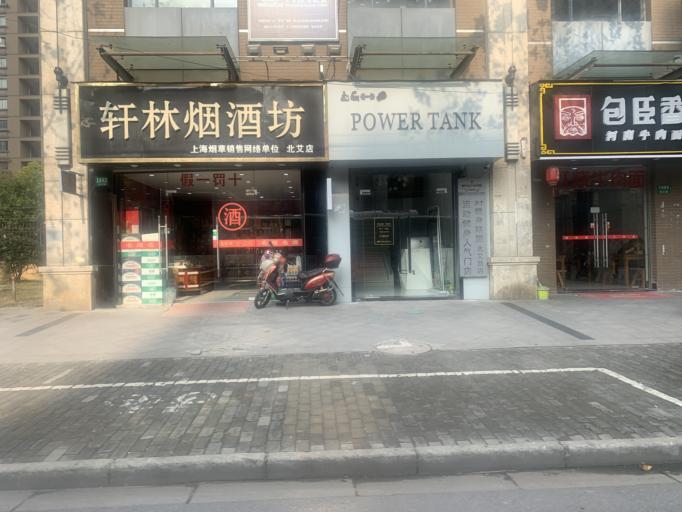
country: CN
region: Shanghai Shi
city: Huamu
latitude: 31.1823
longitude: 121.5195
